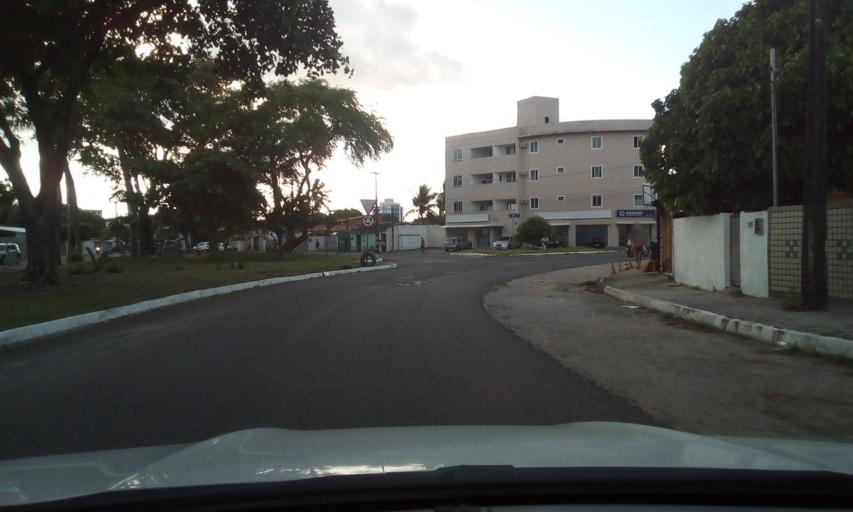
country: BR
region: Paraiba
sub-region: Joao Pessoa
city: Joao Pessoa
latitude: -7.1112
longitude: -34.8578
